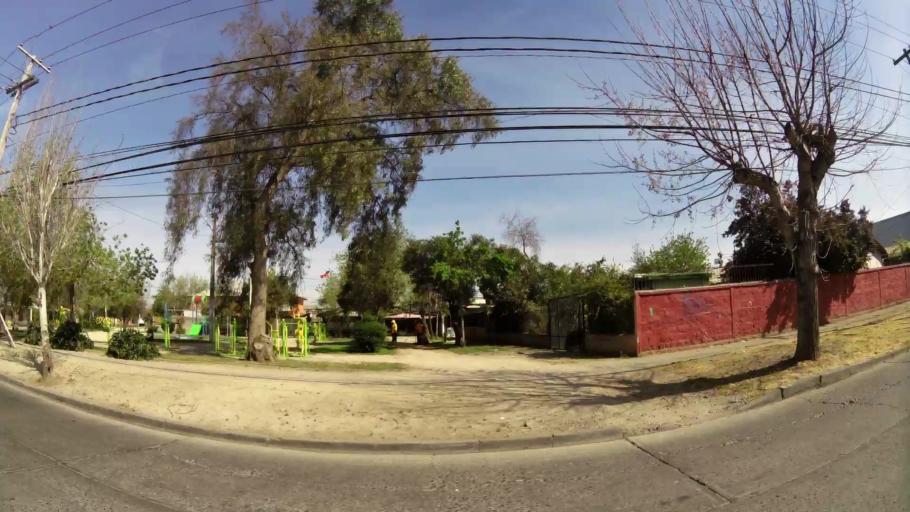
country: CL
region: Santiago Metropolitan
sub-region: Provincia de Santiago
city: La Pintana
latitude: -33.5356
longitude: -70.5990
